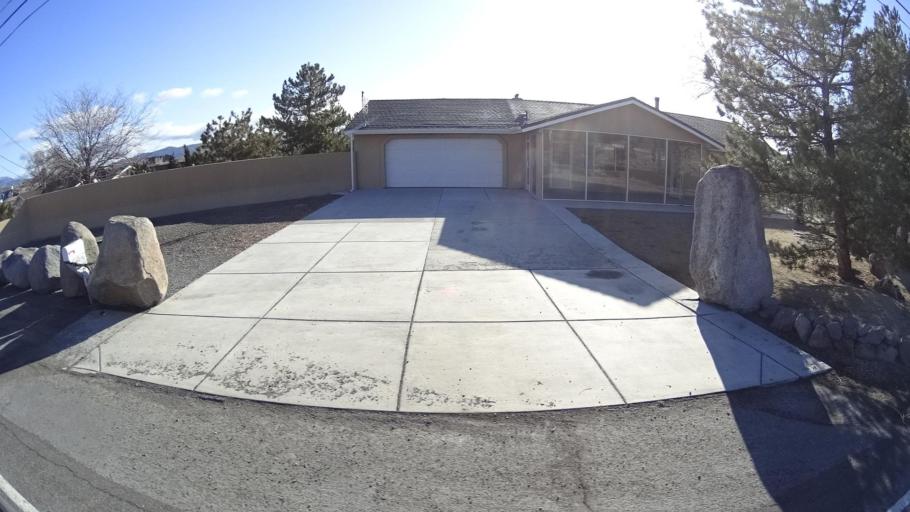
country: US
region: Nevada
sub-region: Washoe County
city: Cold Springs
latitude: 39.6644
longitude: -119.9224
